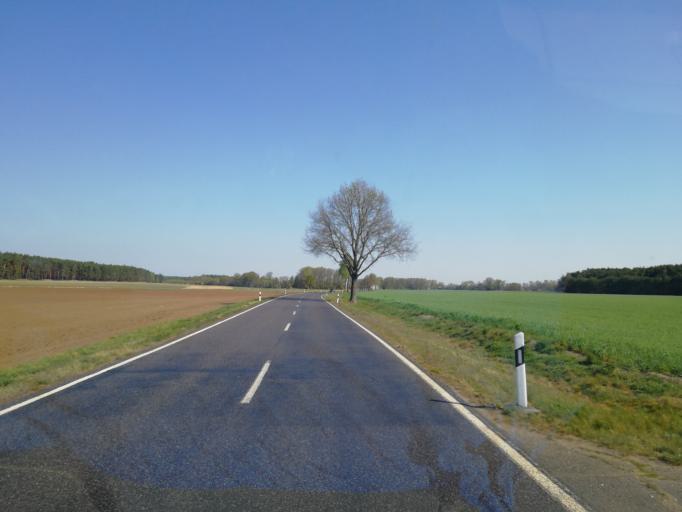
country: DE
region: Brandenburg
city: Crinitz
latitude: 51.7468
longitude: 13.8558
